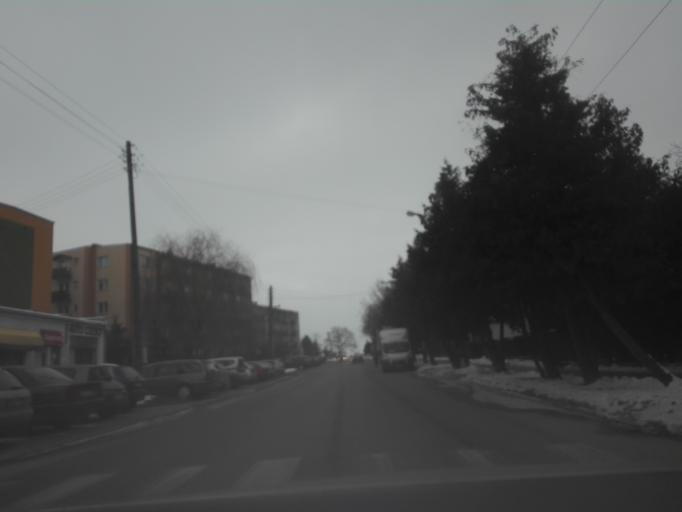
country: PL
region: Lublin Voivodeship
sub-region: Powiat hrubieszowski
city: Hrubieszow
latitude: 50.8017
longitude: 23.8960
